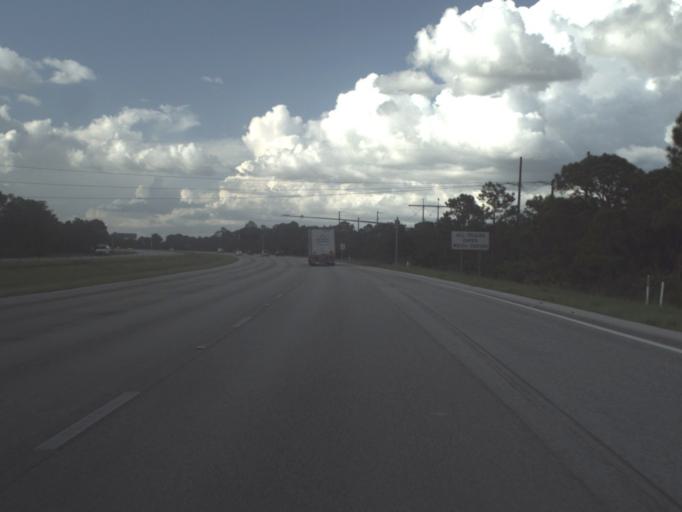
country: US
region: Florida
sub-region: Charlotte County
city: Charlotte Park
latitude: 26.8641
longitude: -81.9721
